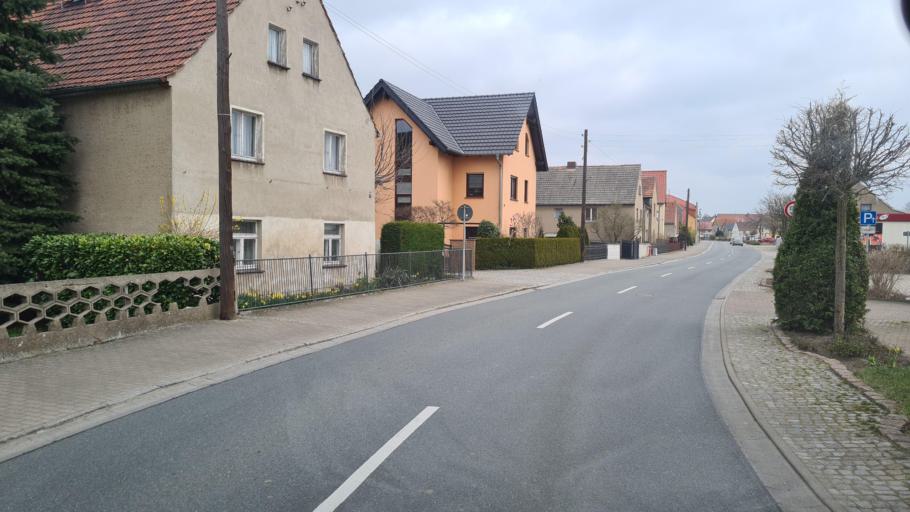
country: DE
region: Saxony
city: Zabeltitz
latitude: 51.3877
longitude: 13.4741
